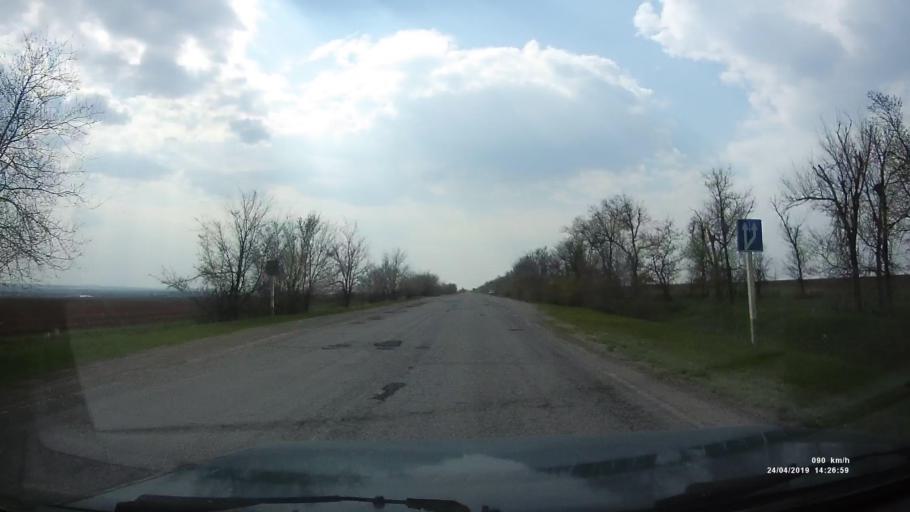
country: RU
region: Kalmykiya
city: Arshan'
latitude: 46.3341
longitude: 44.0518
